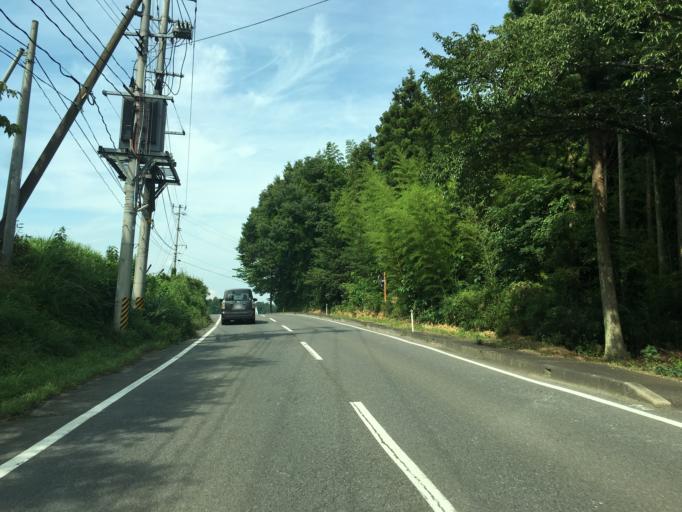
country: JP
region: Fukushima
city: Sukagawa
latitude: 37.2771
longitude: 140.4220
